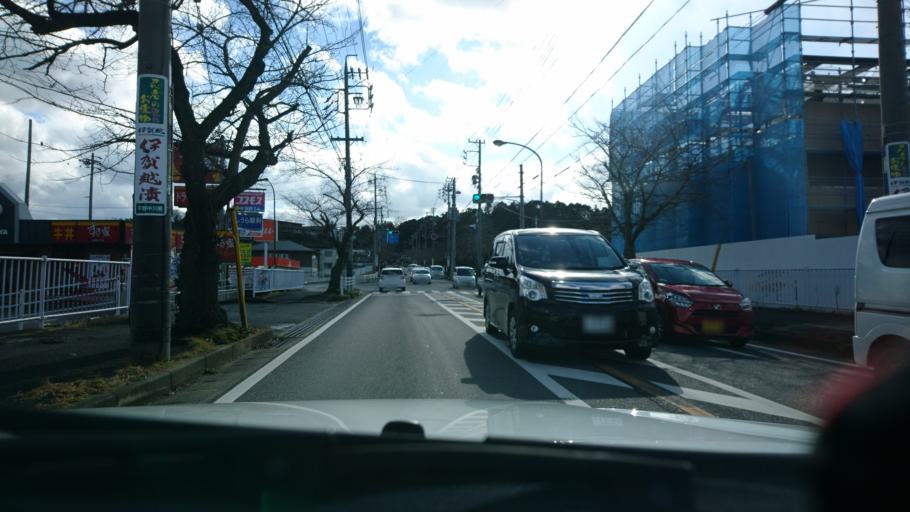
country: JP
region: Mie
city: Ueno-ebisumachi
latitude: 34.7752
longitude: 136.1297
